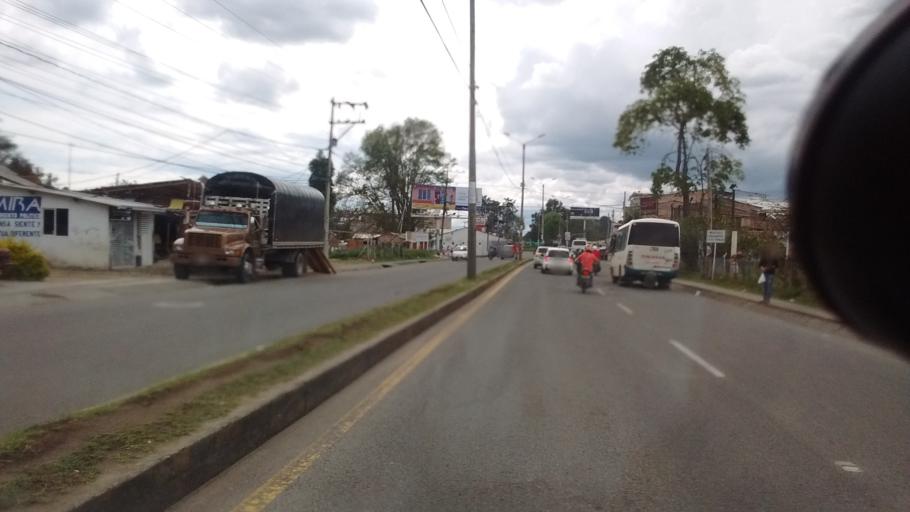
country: CO
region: Cauca
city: Popayan
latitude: 2.4813
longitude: -76.5721
